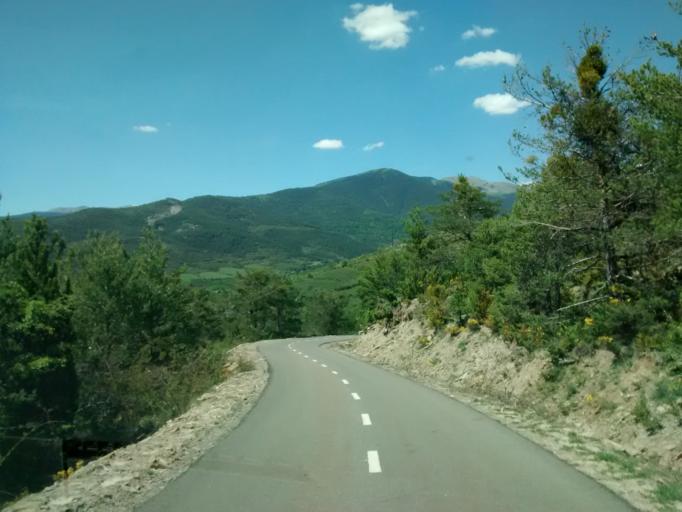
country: ES
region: Aragon
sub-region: Provincia de Huesca
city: Borau
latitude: 42.6745
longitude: -0.6169
